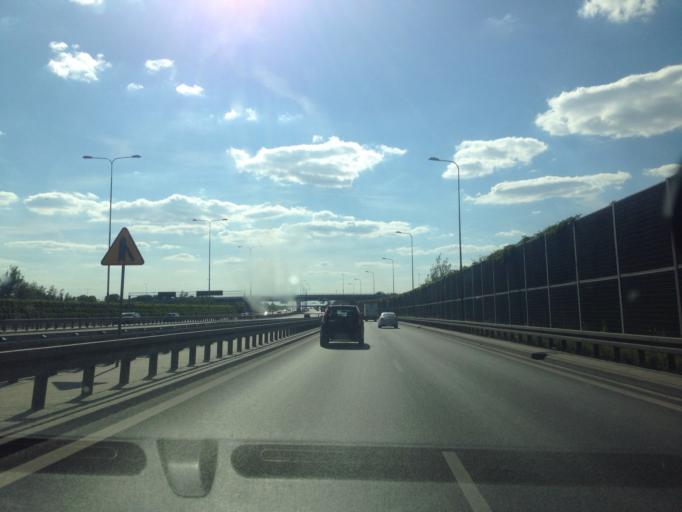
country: PL
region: Masovian Voivodeship
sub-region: Powiat piaseczynski
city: Mysiadlo
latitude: 52.1397
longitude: 21.0112
